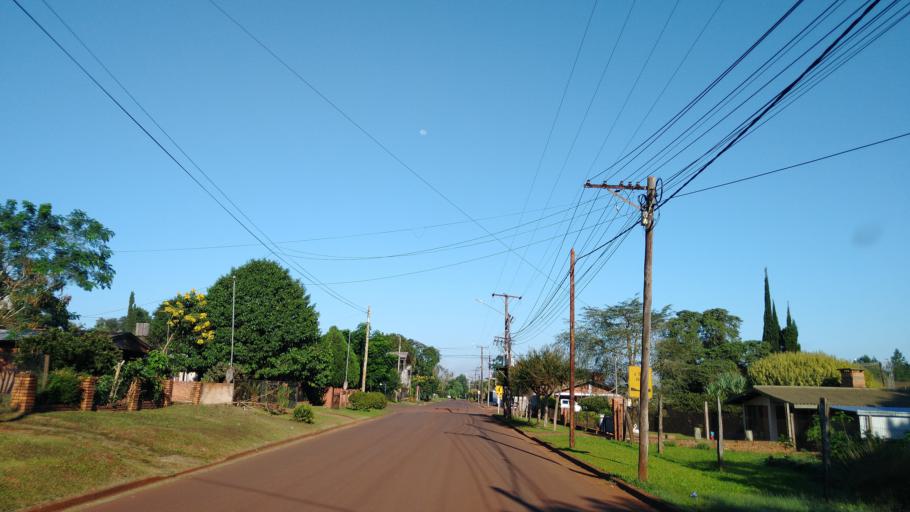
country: AR
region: Misiones
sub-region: Departamento de Montecarlo
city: Montecarlo
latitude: -26.5651
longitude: -54.7569
